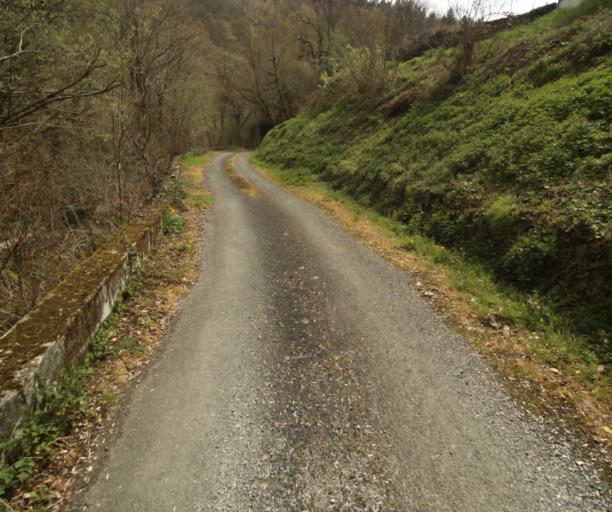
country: FR
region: Limousin
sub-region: Departement de la Correze
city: Tulle
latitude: 45.2722
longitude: 1.7959
